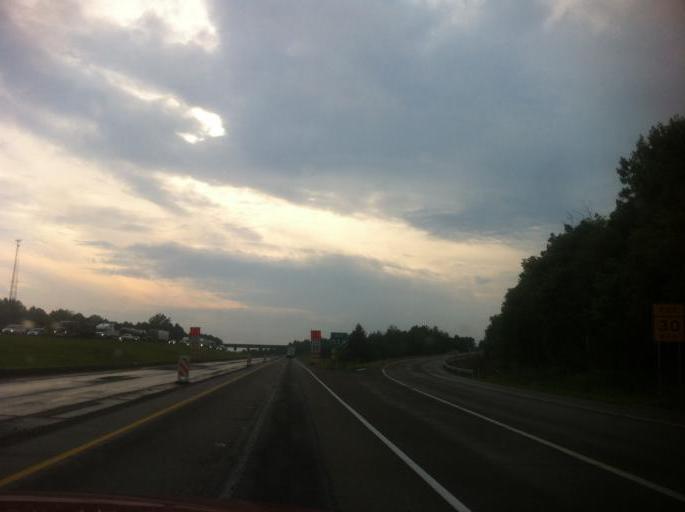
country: US
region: Pennsylvania
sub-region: Clarion County
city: Knox
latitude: 41.1840
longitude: -79.5361
